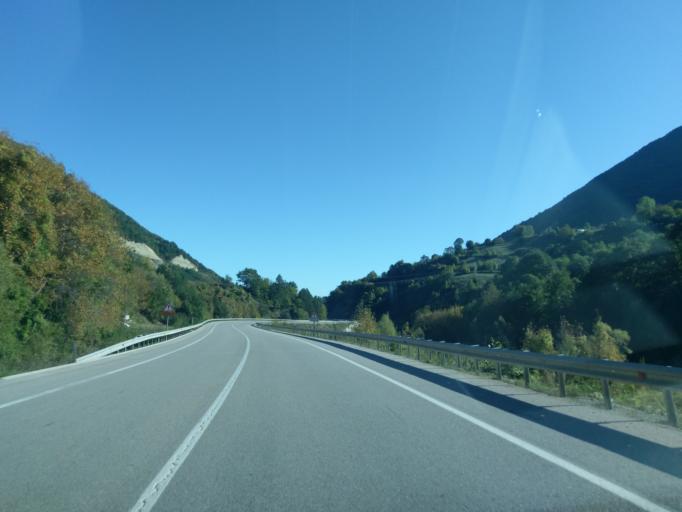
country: TR
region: Sinop
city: Kabali
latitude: 41.7840
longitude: 34.9946
